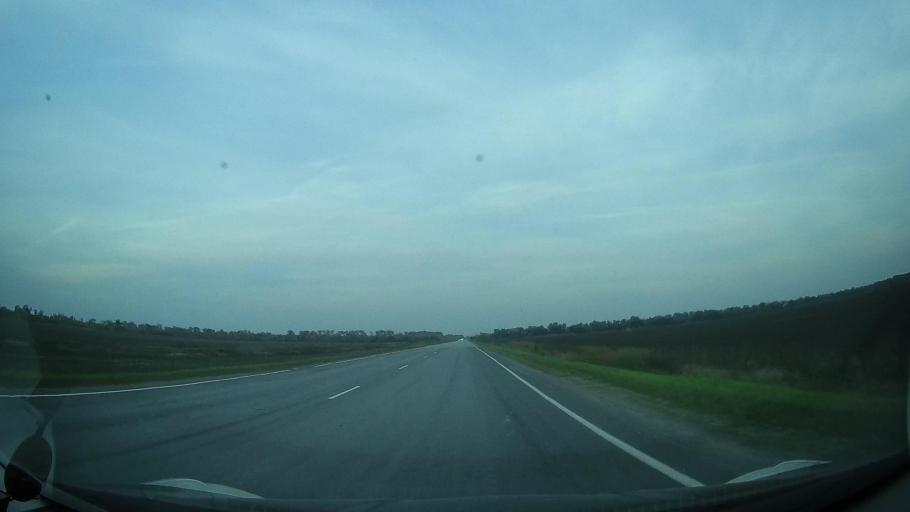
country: RU
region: Rostov
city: Ol'ginskaya
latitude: 47.1303
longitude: 39.9192
